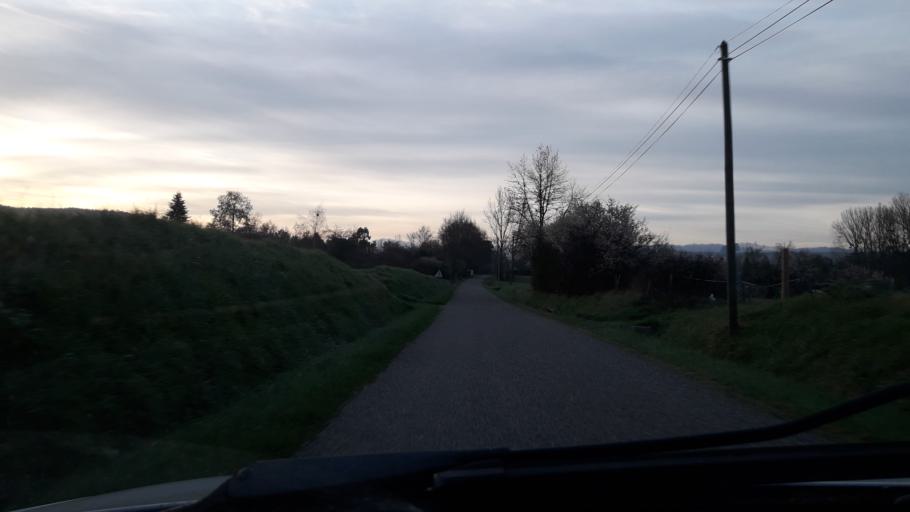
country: FR
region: Midi-Pyrenees
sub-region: Departement de la Haute-Garonne
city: Montesquieu-Volvestre
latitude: 43.1715
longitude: 1.2714
